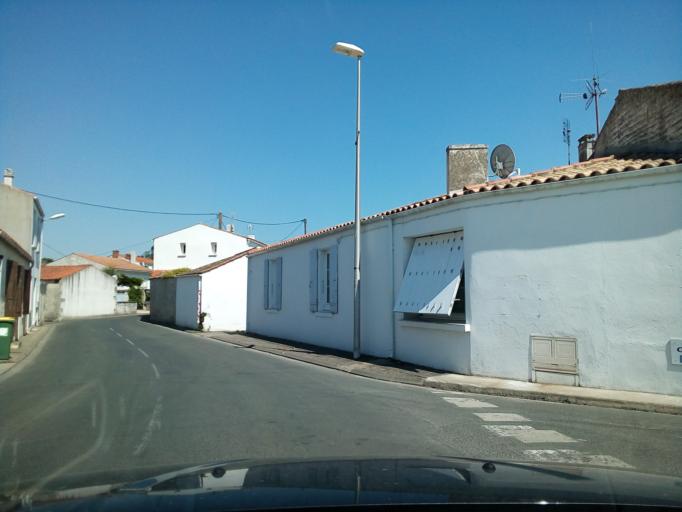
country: FR
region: Poitou-Charentes
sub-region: Departement de la Charente-Maritime
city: Boyard-Ville
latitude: 45.9710
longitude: -1.2950
